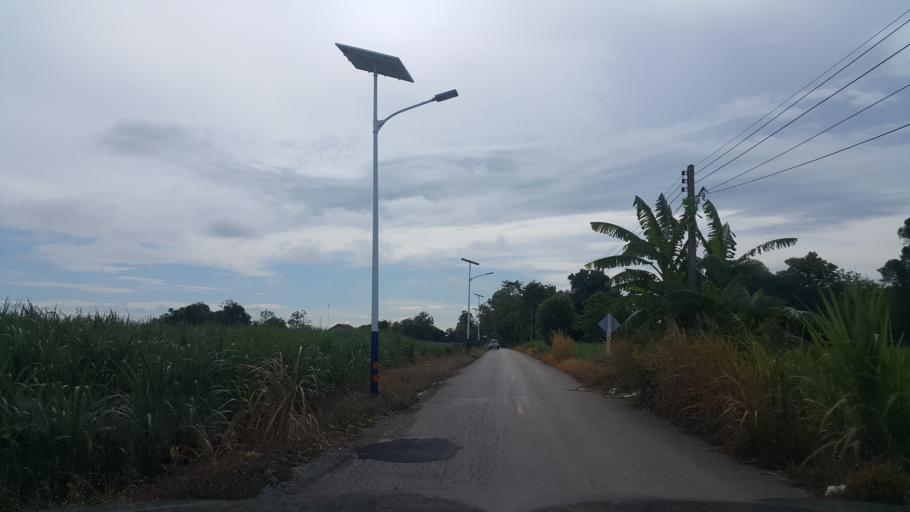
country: TH
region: Sukhothai
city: Sawankhalok
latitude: 17.2651
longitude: 99.9095
